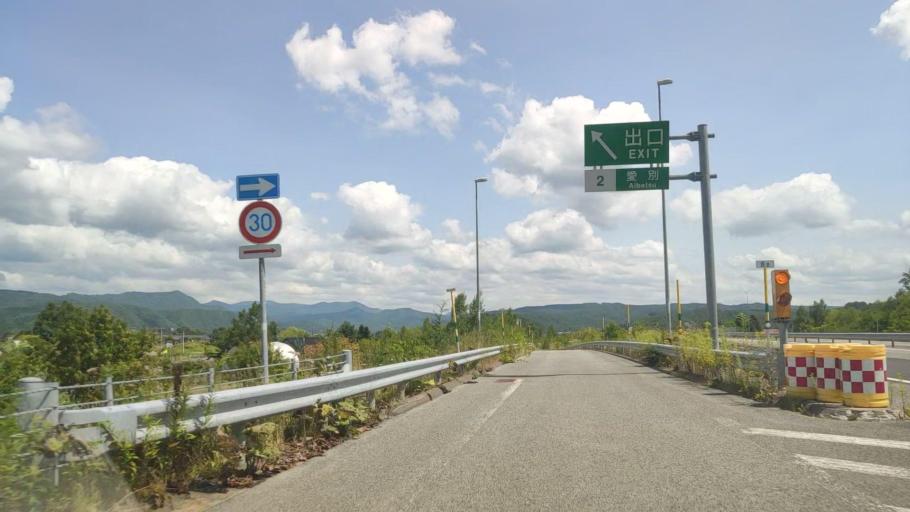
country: JP
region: Hokkaido
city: Kamikawa
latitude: 43.8955
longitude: 142.5700
